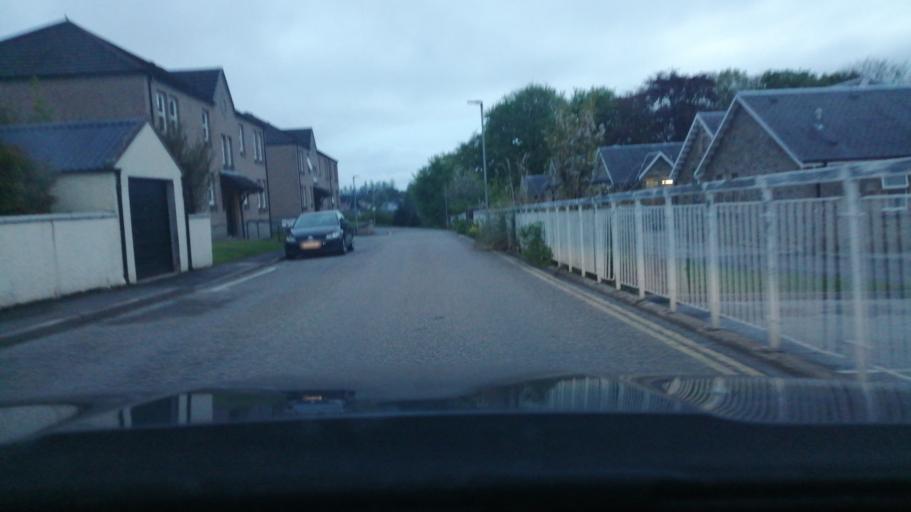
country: GB
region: Scotland
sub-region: Moray
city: Keith
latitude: 57.5417
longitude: -2.9546
